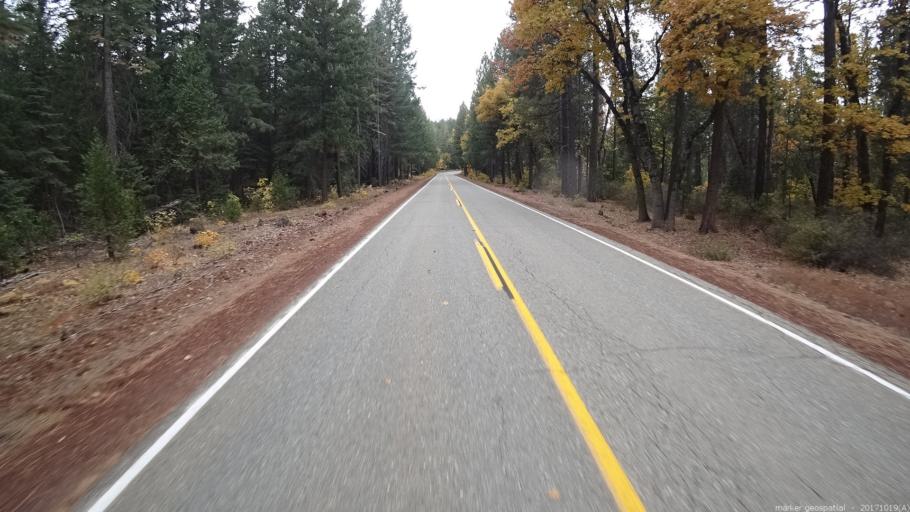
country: US
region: California
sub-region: Shasta County
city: Burney
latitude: 41.1183
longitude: -121.5860
